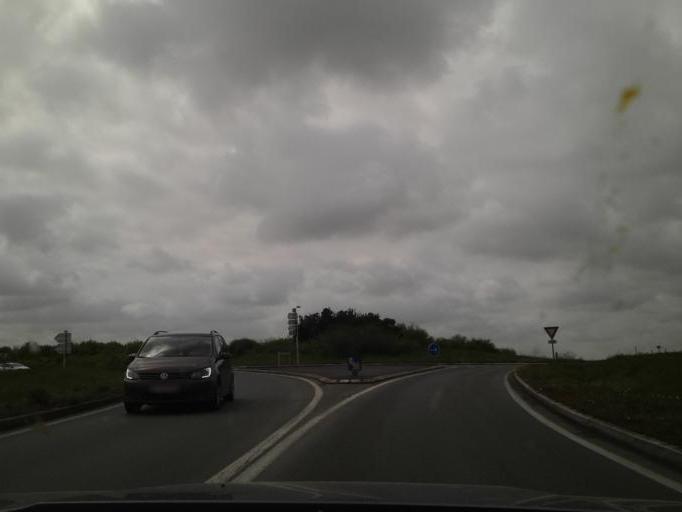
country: FR
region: Pays de la Loire
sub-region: Departement de la Vendee
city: Fontenay-le-Comte
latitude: 46.4382
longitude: -0.8237
